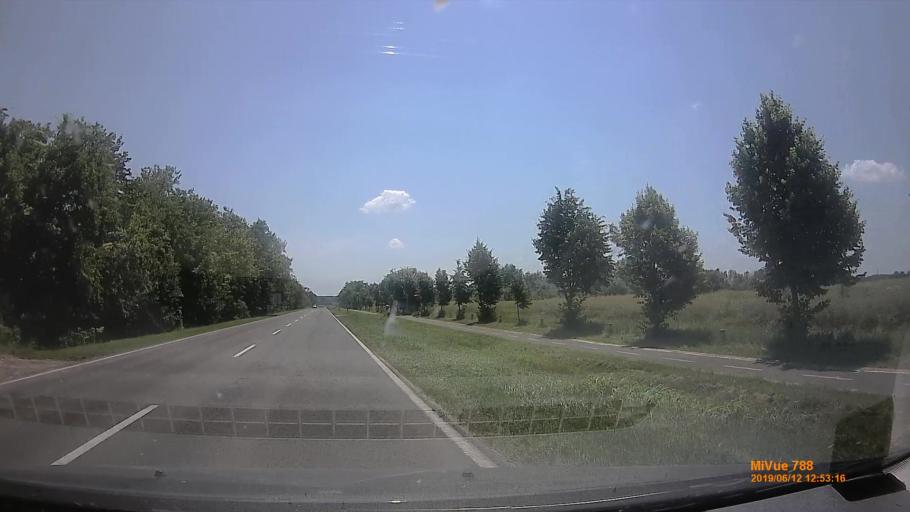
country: HU
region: Bacs-Kiskun
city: Kiskunfelegyhaza
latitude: 46.6840
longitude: 19.8519
